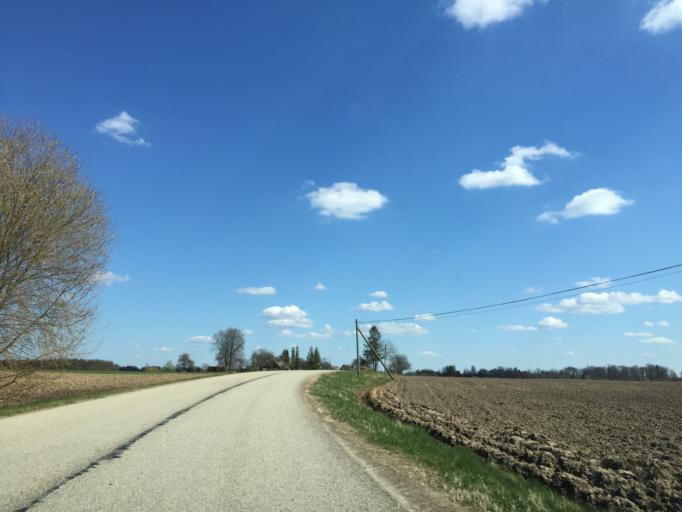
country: LV
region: Seja
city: Loja
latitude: 57.2650
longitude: 24.5754
